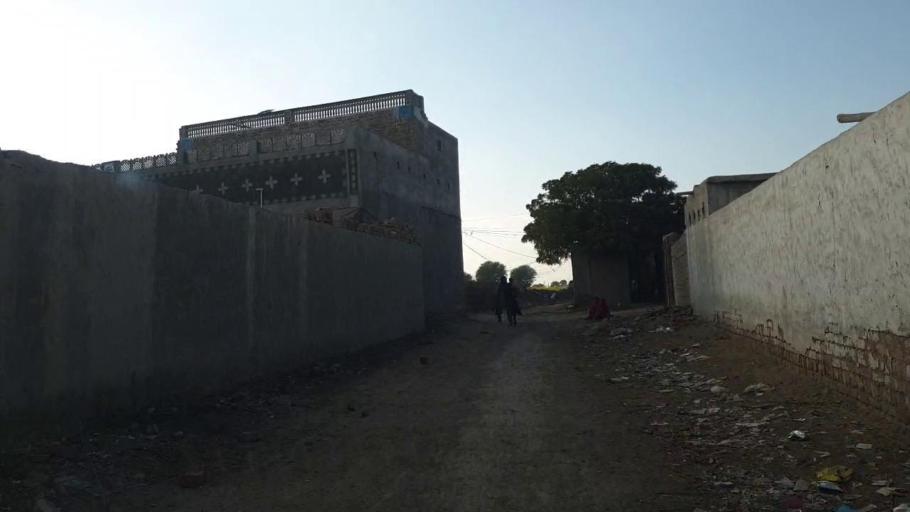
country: PK
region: Sindh
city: Shahpur Chakar
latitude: 26.1311
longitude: 68.5586
